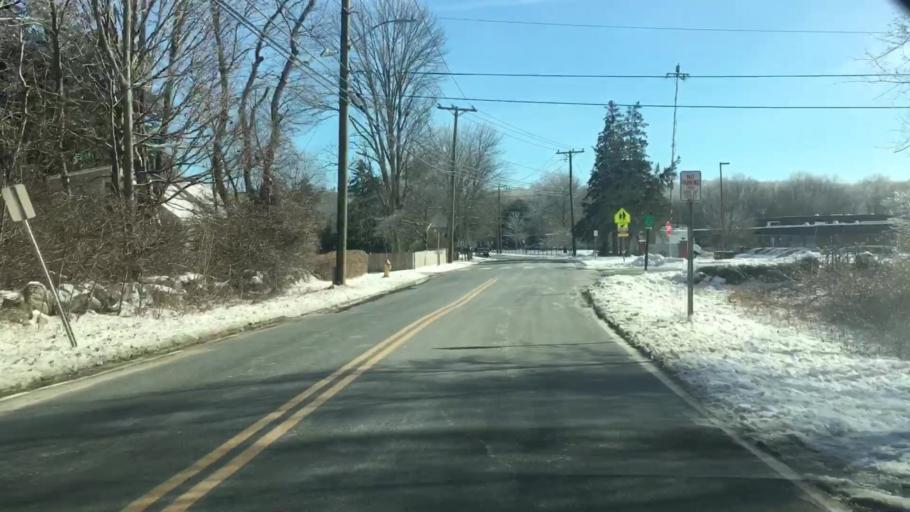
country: US
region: Connecticut
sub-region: Fairfield County
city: Newtown
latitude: 41.3470
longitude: -73.2314
